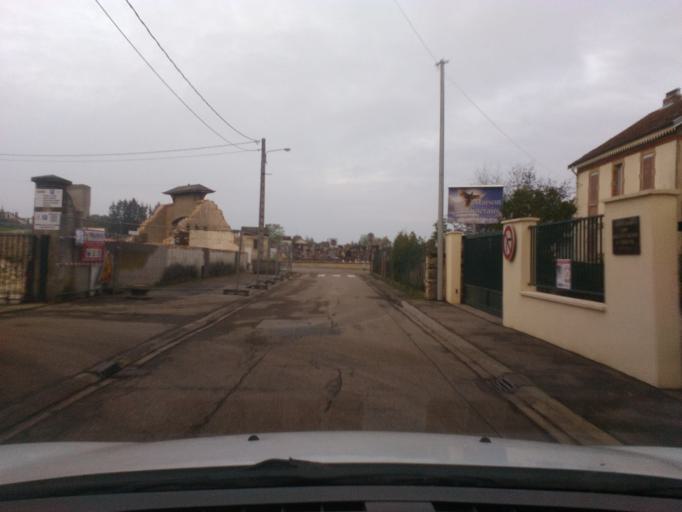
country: FR
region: Lorraine
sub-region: Departement des Vosges
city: Mirecourt
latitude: 48.3065
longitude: 6.1321
